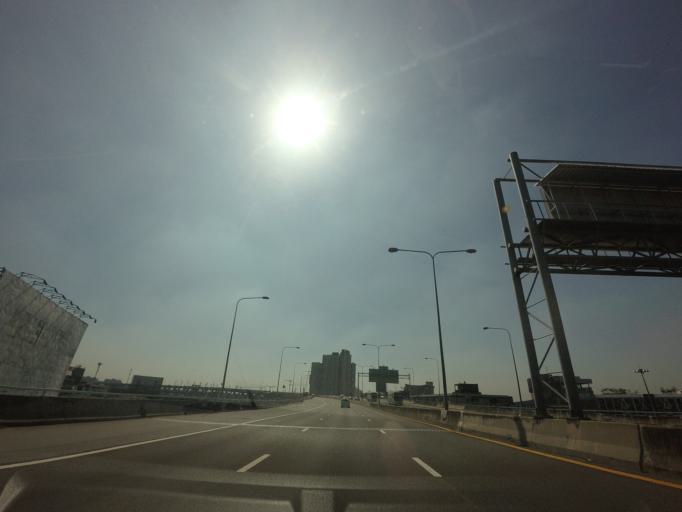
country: TH
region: Bangkok
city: Phra Khanong
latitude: 13.6780
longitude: 100.6041
